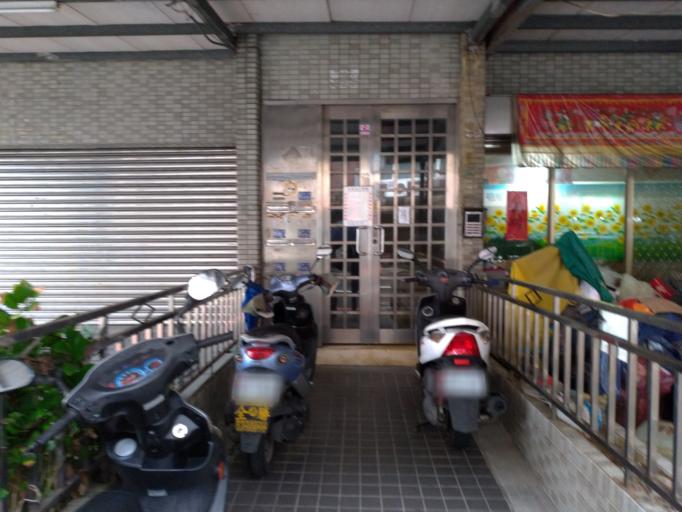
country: TW
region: Taiwan
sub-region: Keelung
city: Keelung
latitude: 25.0875
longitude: 121.6978
